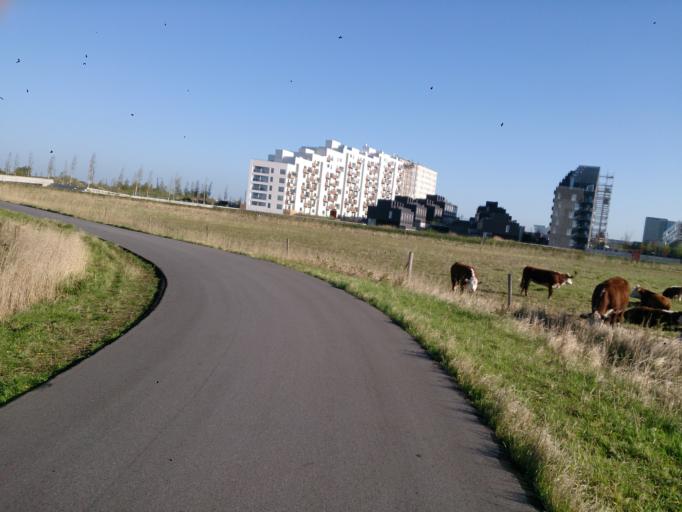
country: DK
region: Capital Region
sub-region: Tarnby Kommune
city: Tarnby
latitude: 55.6145
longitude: 12.5686
